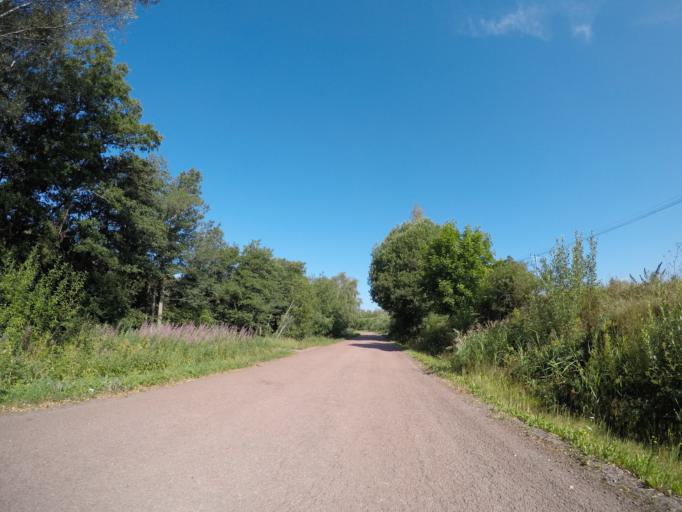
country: AX
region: Alands landsbygd
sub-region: Finstroem
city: Finstroem
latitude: 60.2694
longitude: 19.9268
